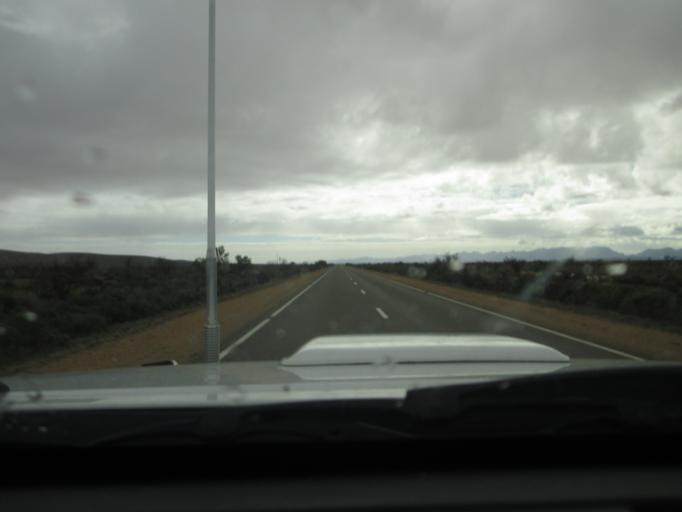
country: AU
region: South Australia
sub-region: Flinders Ranges
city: Quorn
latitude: -31.5121
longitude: 138.4280
